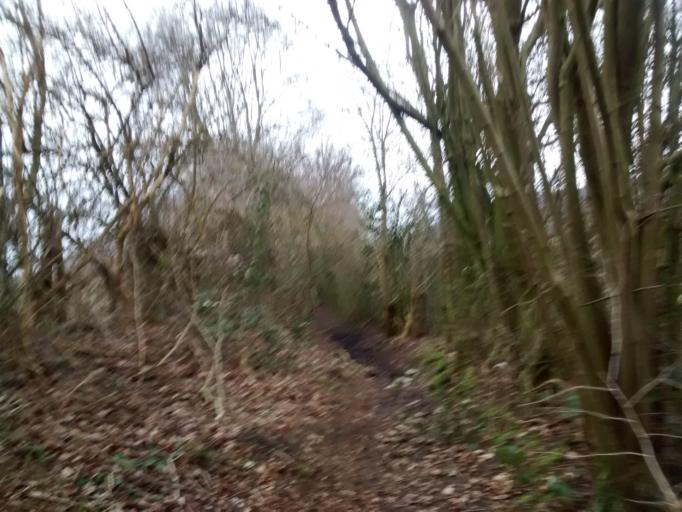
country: NL
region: Limburg
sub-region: Gemeente Vaals
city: Vaals
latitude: 50.7533
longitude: 6.0328
